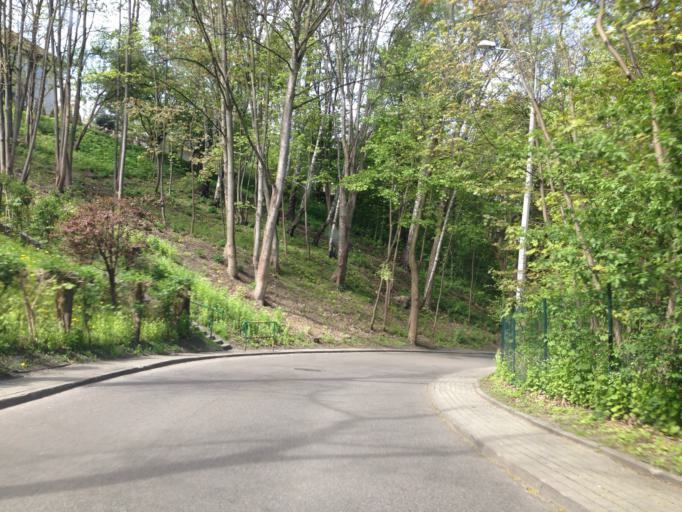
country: PL
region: Pomeranian Voivodeship
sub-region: Gdynia
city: Gdynia
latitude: 54.5135
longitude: 18.5475
